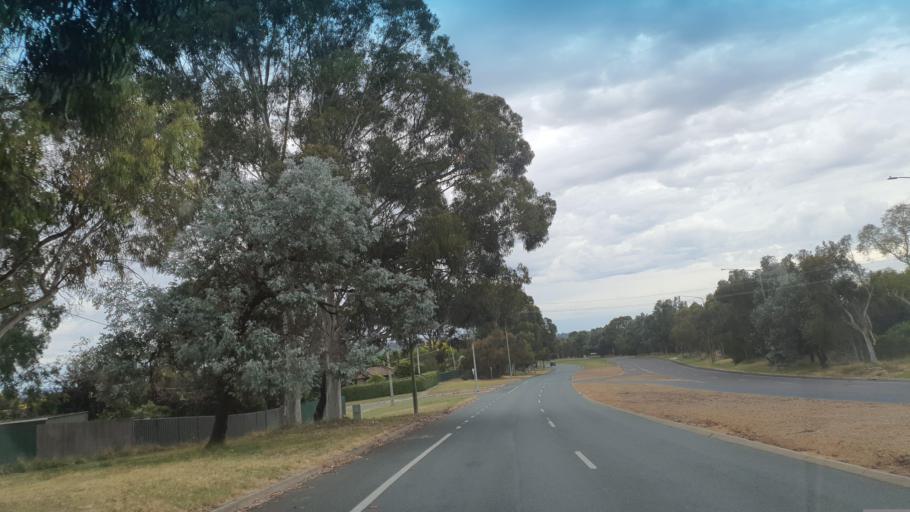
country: AU
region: Australian Capital Territory
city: Macquarie
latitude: -35.2378
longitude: 149.0312
